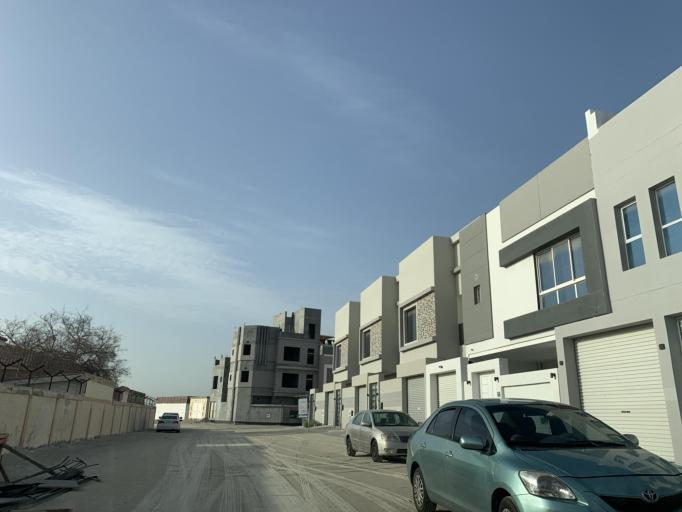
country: BH
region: Northern
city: Madinat `Isa
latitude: 26.1781
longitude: 50.5819
